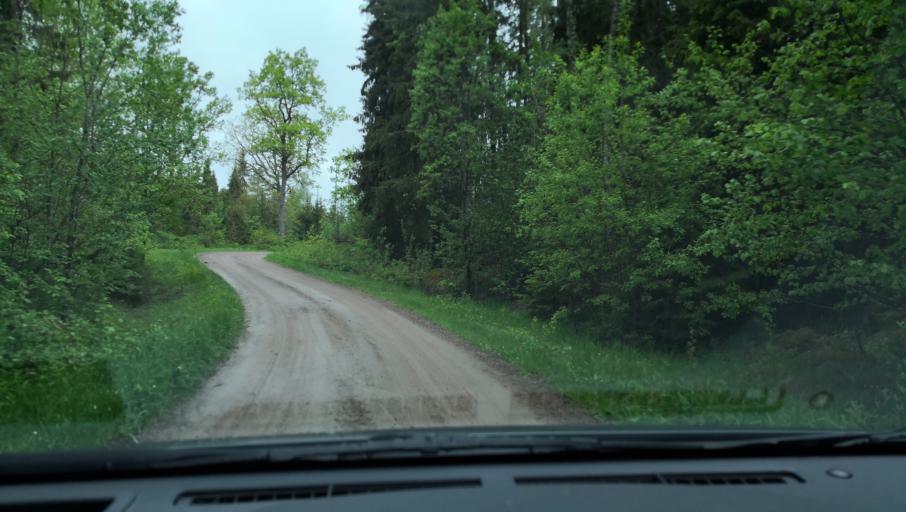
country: SE
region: Uppsala
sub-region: Enkopings Kommun
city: Orsundsbro
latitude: 59.9178
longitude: 17.3474
